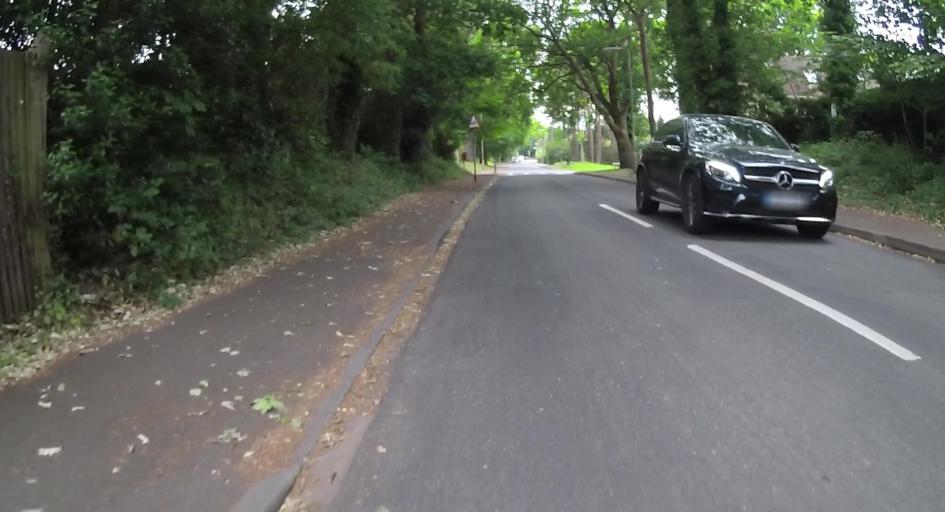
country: GB
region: England
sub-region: Hampshire
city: Fleet
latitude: 51.2600
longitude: -0.8274
